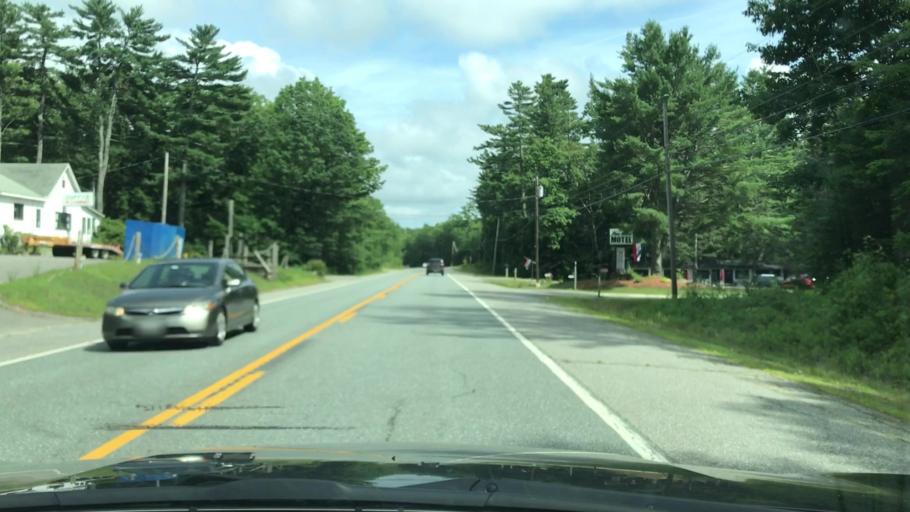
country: US
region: Maine
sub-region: Hancock County
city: Orland
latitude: 44.5657
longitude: -68.6693
